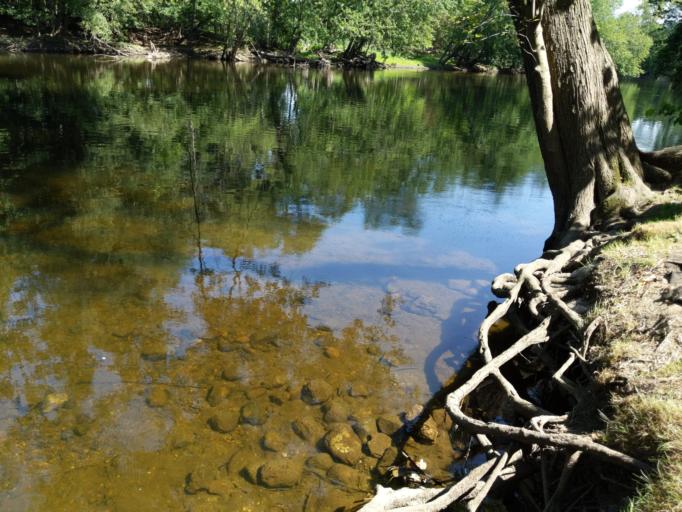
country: US
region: Michigan
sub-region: Eaton County
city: Waverly
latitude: 42.7610
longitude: -84.6561
